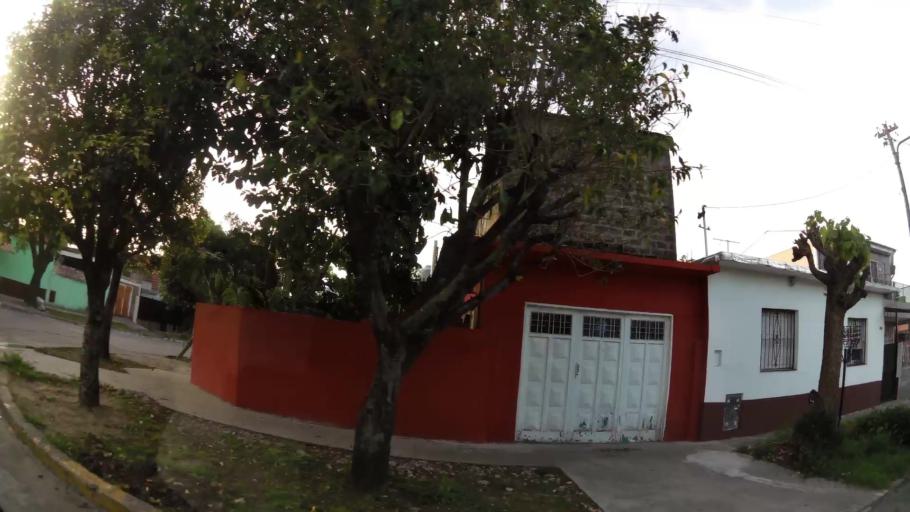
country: AR
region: Buenos Aires
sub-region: Partido de Quilmes
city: Quilmes
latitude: -34.7777
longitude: -58.2043
